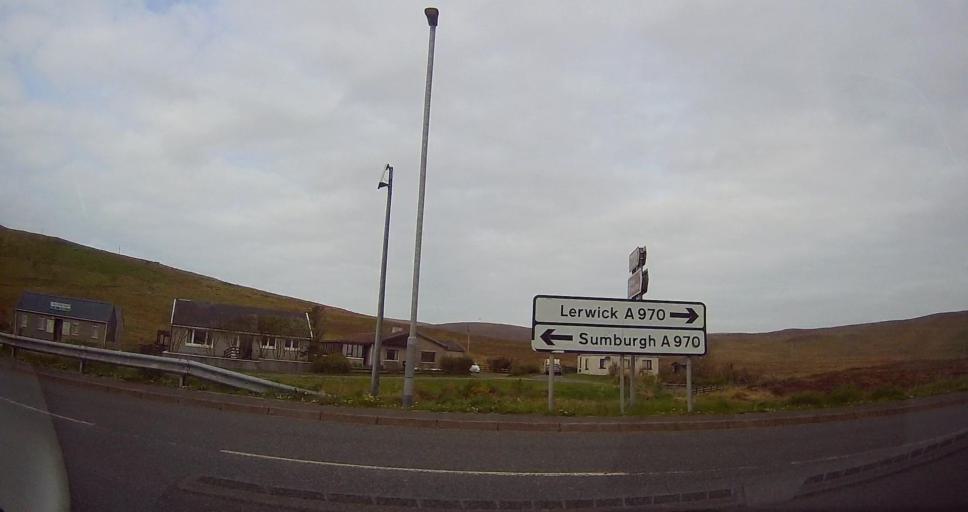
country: GB
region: Scotland
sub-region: Shetland Islands
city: Sandwick
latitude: 60.0559
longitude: -1.2253
